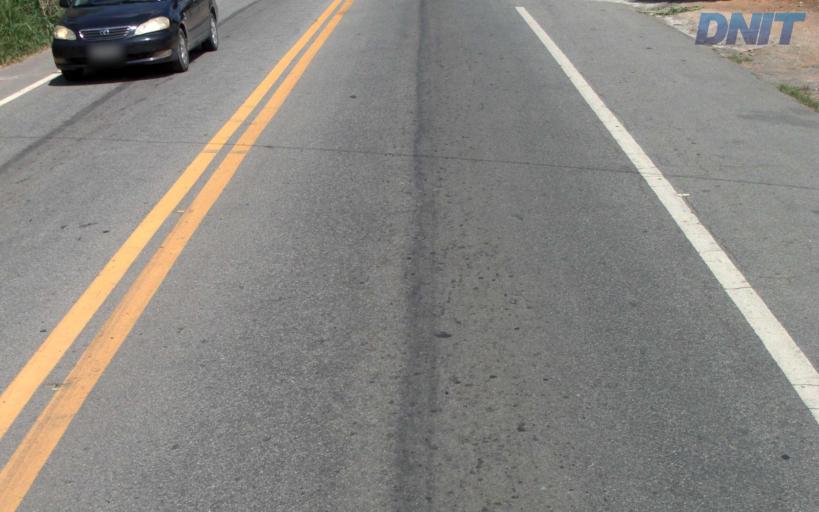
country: BR
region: Minas Gerais
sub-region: Timoteo
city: Timoteo
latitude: -19.5396
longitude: -42.6714
